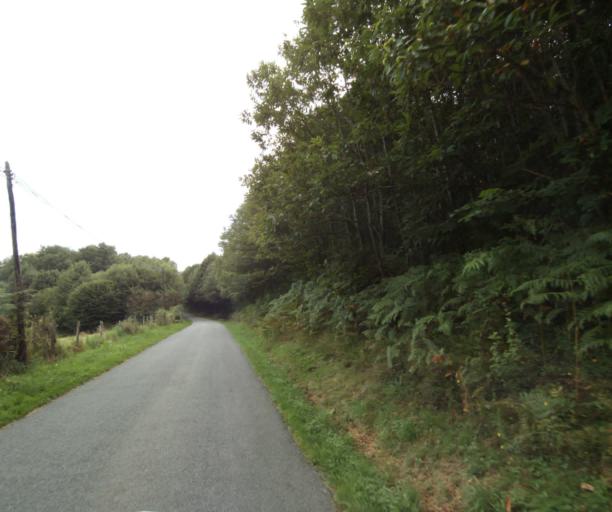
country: FR
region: Limousin
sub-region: Departement de la Correze
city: Sainte-Fortunade
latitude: 45.1964
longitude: 1.8095
